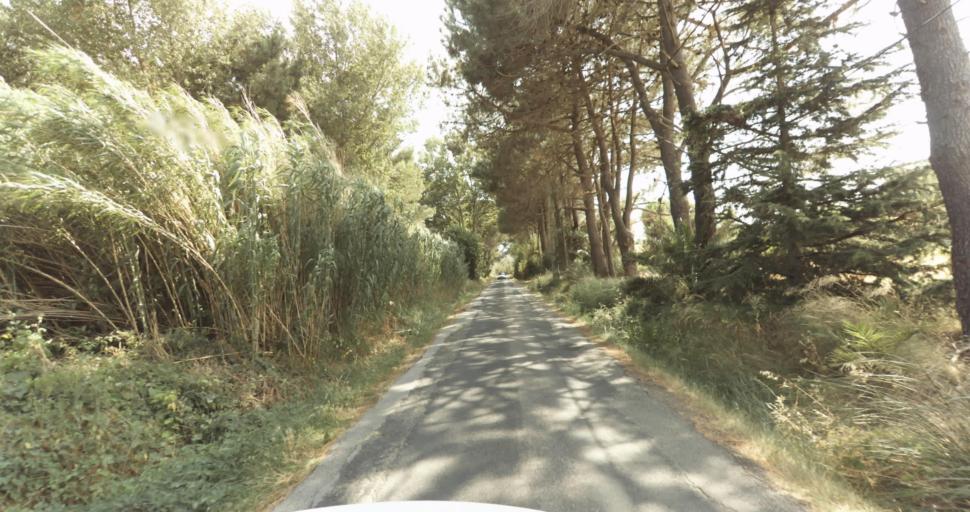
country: FR
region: Languedoc-Roussillon
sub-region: Departement des Pyrenees-Orientales
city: Alenya
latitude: 42.6316
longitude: 2.9990
